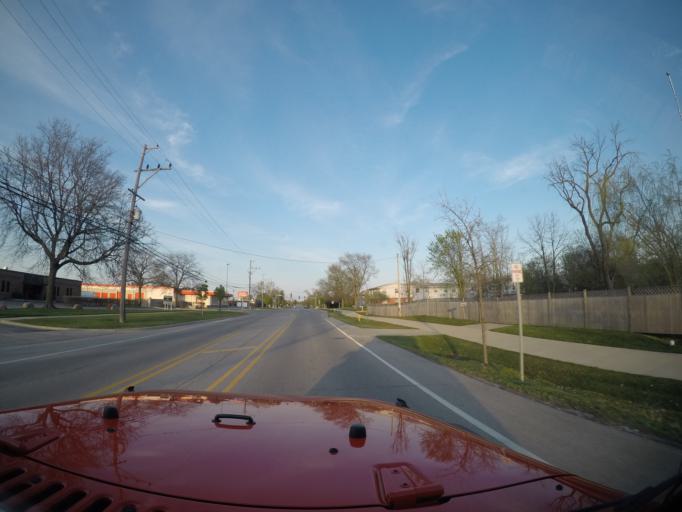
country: US
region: Illinois
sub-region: Cook County
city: Northbrook
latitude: 42.0875
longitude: -87.8414
